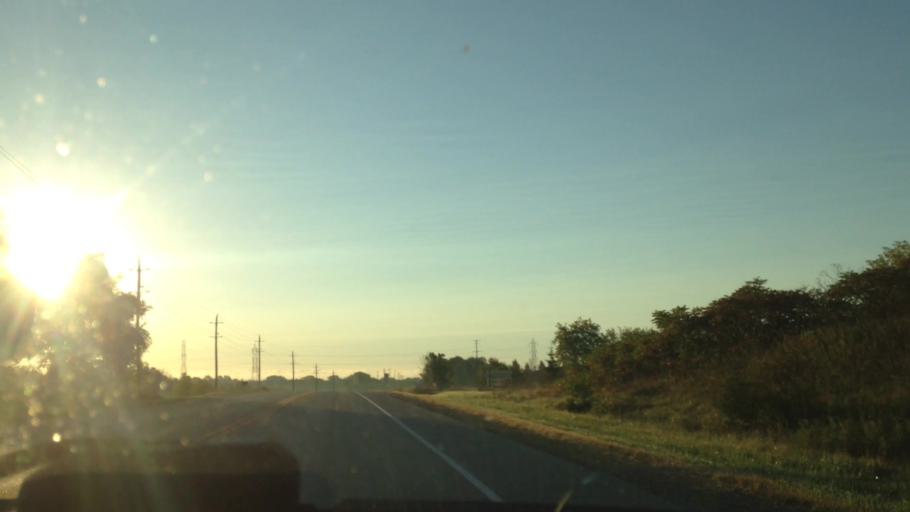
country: US
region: Wisconsin
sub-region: Ozaukee County
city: Saukville
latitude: 43.3888
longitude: -87.9653
